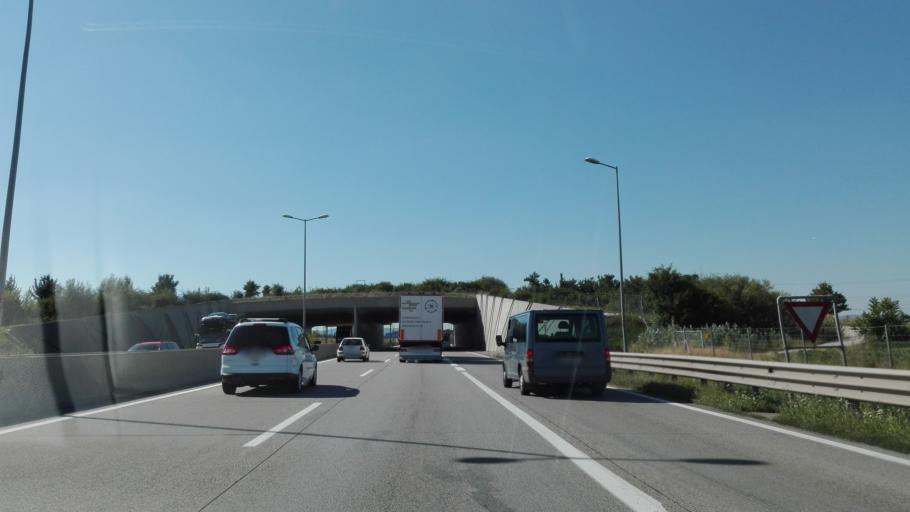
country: AT
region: Lower Austria
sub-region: Politischer Bezirk Wien-Umgebung
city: Leopoldsdorf
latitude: 48.1222
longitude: 16.4070
